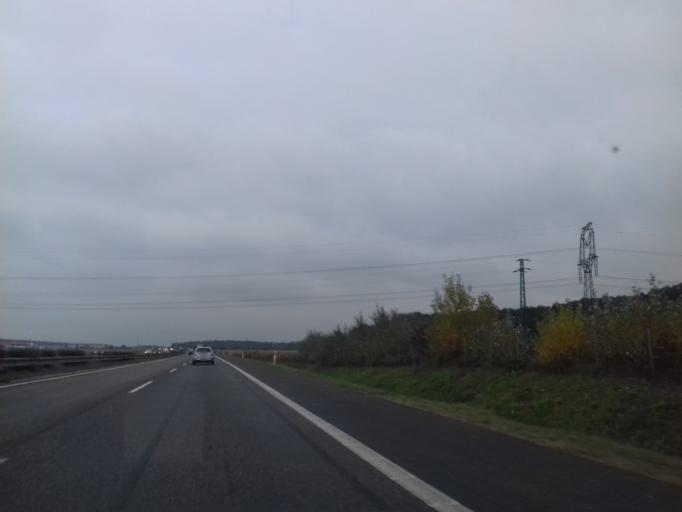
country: SK
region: Bratislavsky
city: Stupava
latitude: 48.3097
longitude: 17.0183
